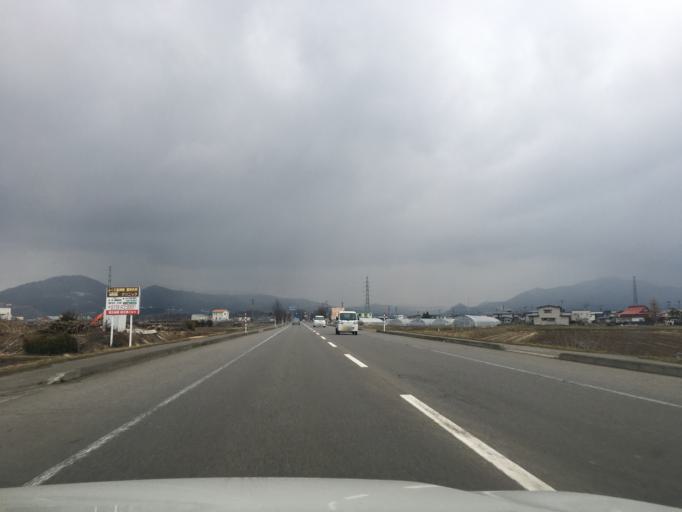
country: JP
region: Aomori
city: Kuroishi
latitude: 40.5790
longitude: 140.5685
